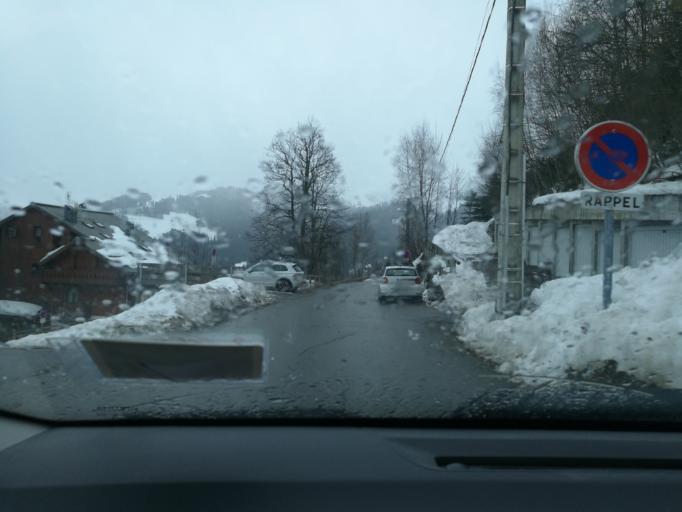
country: FR
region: Rhone-Alpes
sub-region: Departement de la Haute-Savoie
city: Saint-Gervais-les-Bains
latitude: 45.8719
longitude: 6.6896
